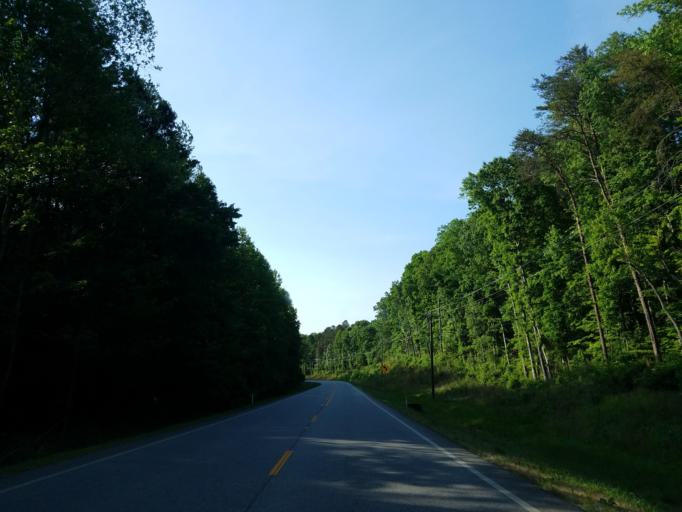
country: US
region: Georgia
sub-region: Whitfield County
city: Dalton
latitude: 34.6719
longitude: -85.0621
